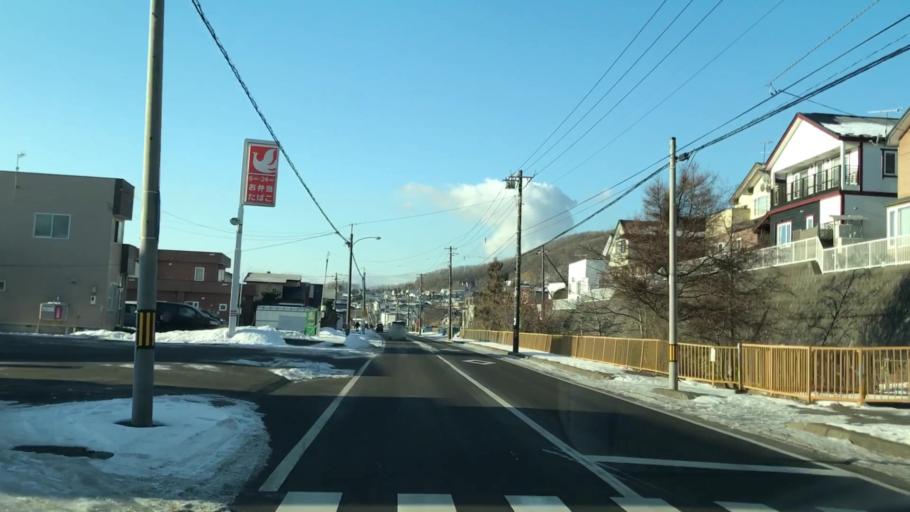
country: JP
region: Hokkaido
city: Muroran
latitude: 42.3726
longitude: 141.0552
